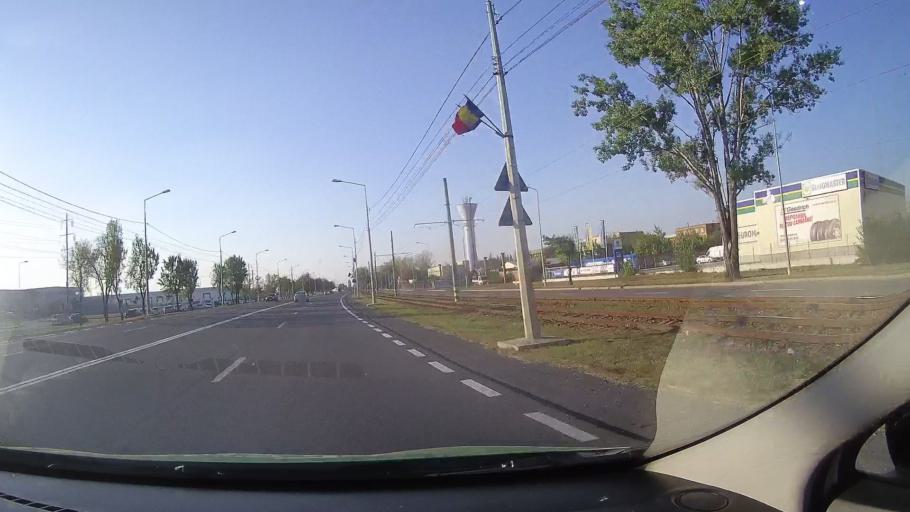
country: RO
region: Bihor
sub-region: Comuna Santandrei
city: Santandrei
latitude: 47.0851
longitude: 21.8833
